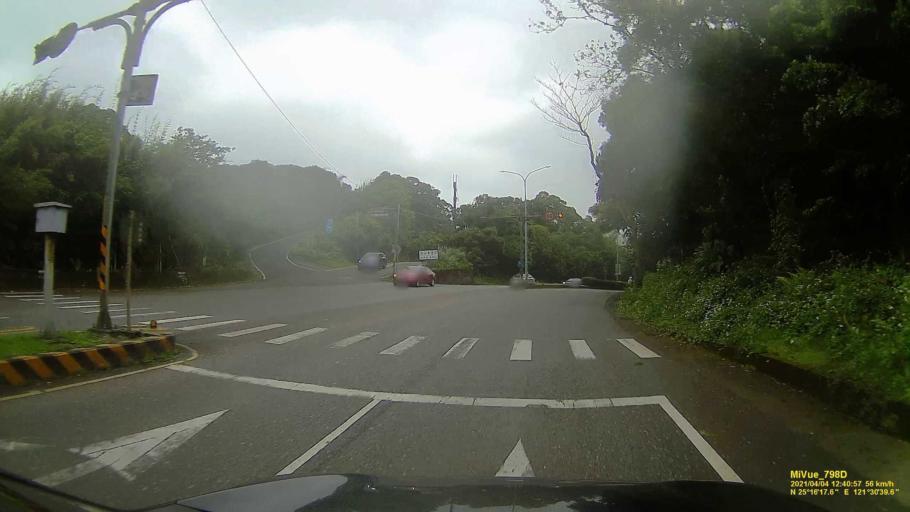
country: TW
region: Taipei
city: Taipei
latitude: 25.2713
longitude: 121.5109
